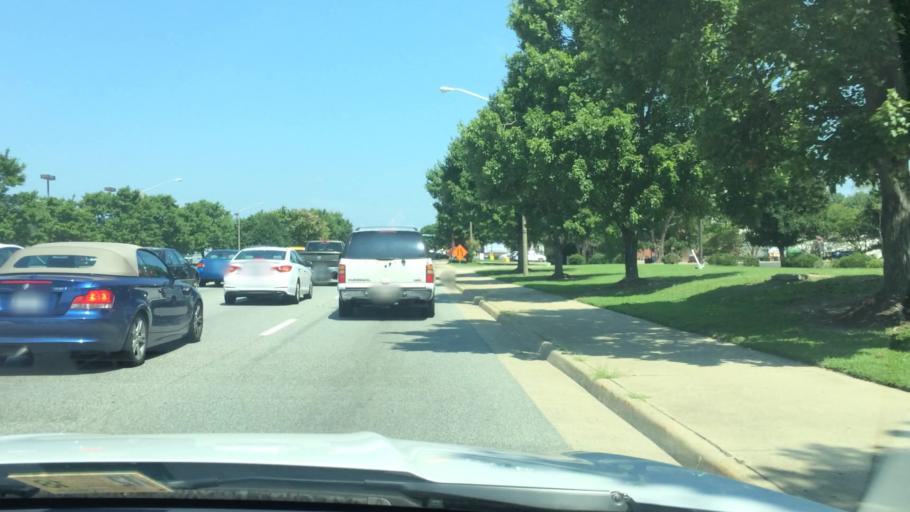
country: US
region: Virginia
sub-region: York County
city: Yorktown
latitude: 37.1331
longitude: -76.5157
